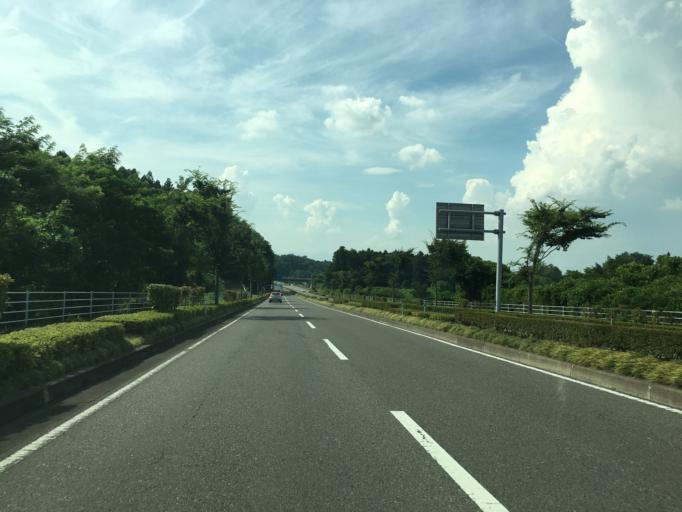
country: JP
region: Fukushima
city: Sukagawa
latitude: 37.2593
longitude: 140.4213
